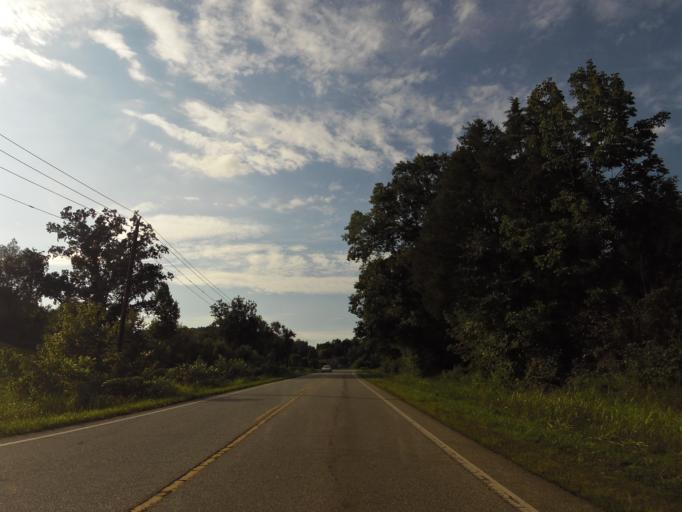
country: US
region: Tennessee
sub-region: Monroe County
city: Vonore
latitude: 35.6272
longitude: -84.3125
